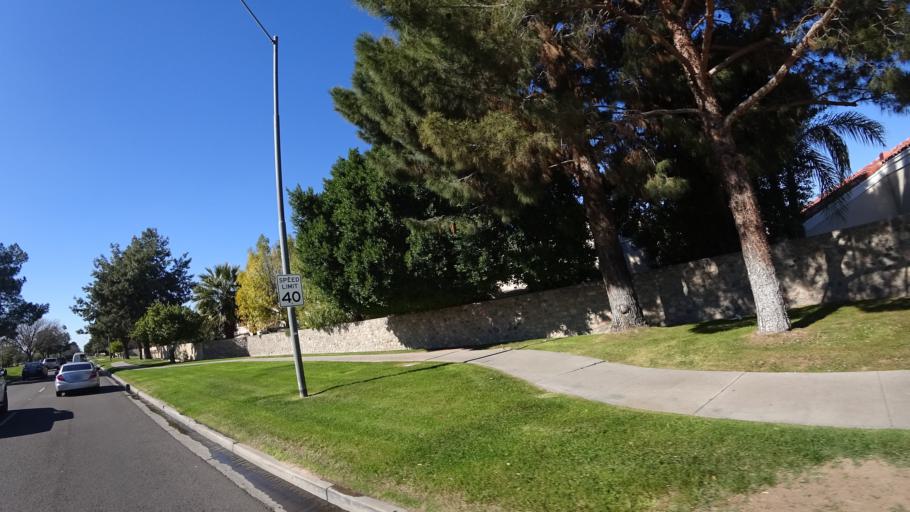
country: US
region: Arizona
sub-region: Maricopa County
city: Peoria
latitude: 33.6529
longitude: -112.2037
